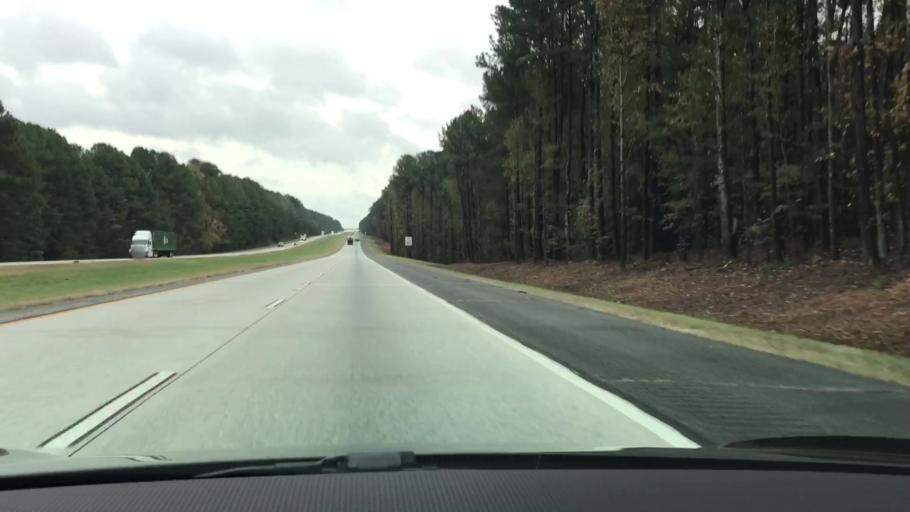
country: US
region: Georgia
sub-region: Taliaferro County
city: Crawfordville
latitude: 33.5211
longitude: -82.8694
